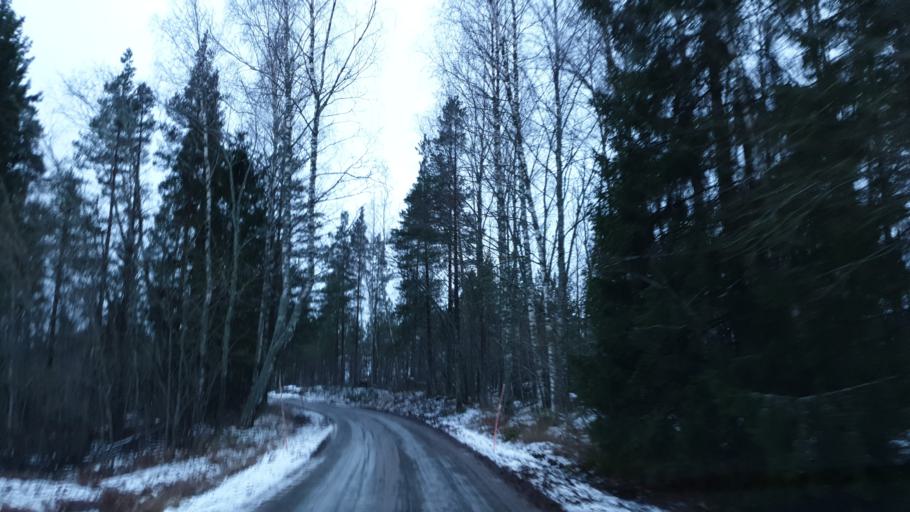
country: SE
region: Uppsala
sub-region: Tierps Kommun
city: Tierp
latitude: 60.3451
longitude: 17.4682
